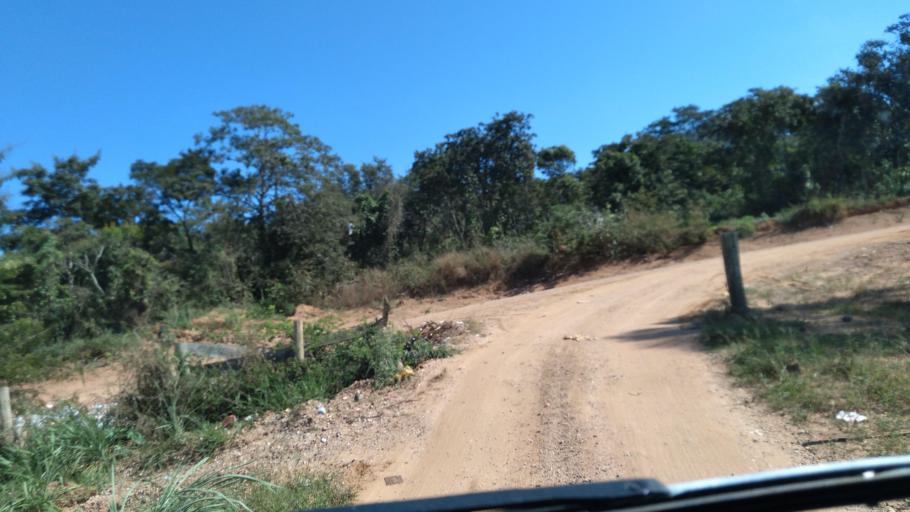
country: BR
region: Goias
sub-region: Mineiros
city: Mineiros
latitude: -17.5977
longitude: -52.4980
